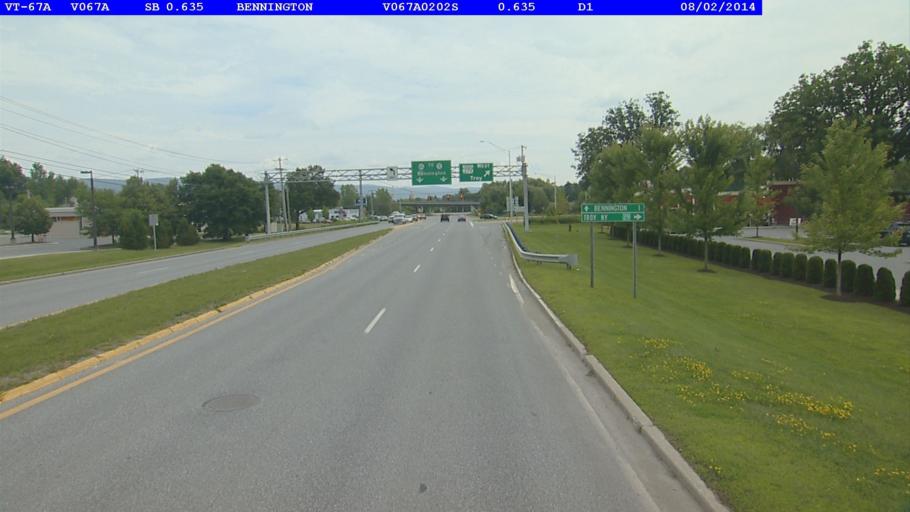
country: US
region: Vermont
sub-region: Bennington County
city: North Bennington
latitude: 42.9076
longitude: -73.2201
